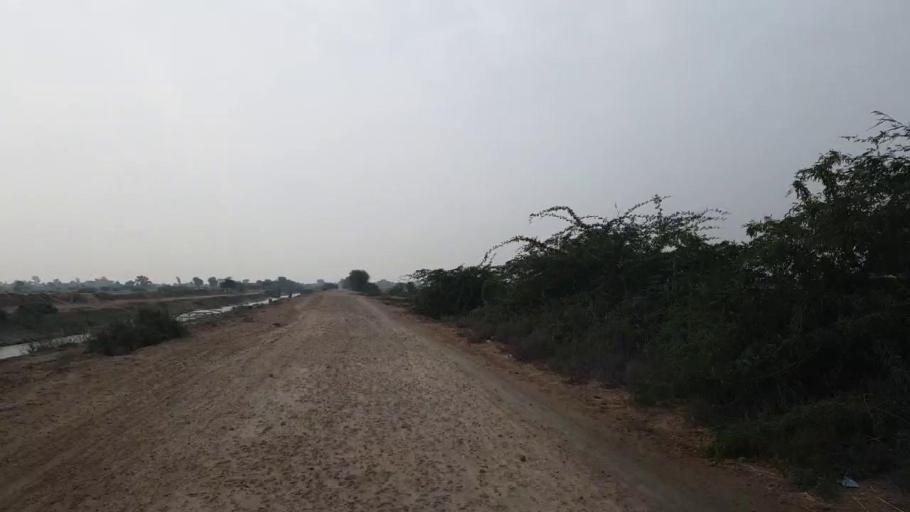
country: PK
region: Sindh
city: Kario
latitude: 24.8898
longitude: 68.5261
